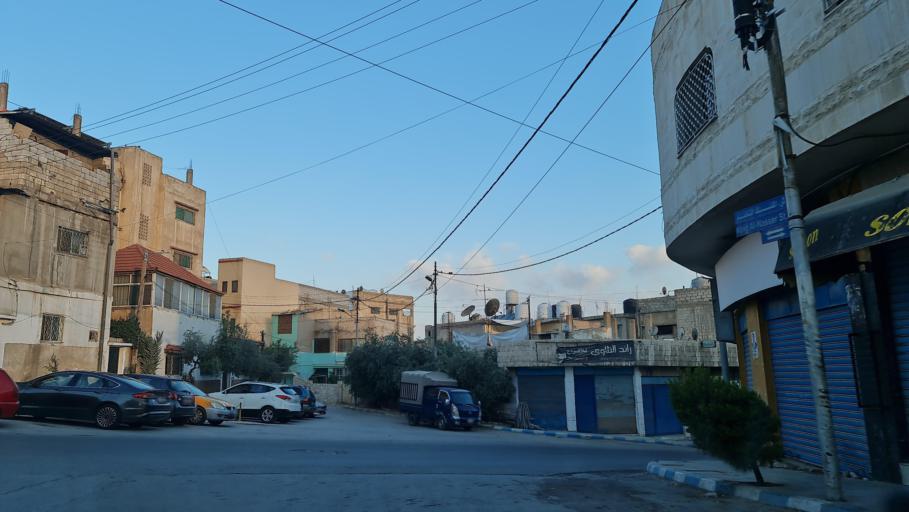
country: JO
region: Zarqa
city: Zarqa
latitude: 32.0762
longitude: 36.0814
